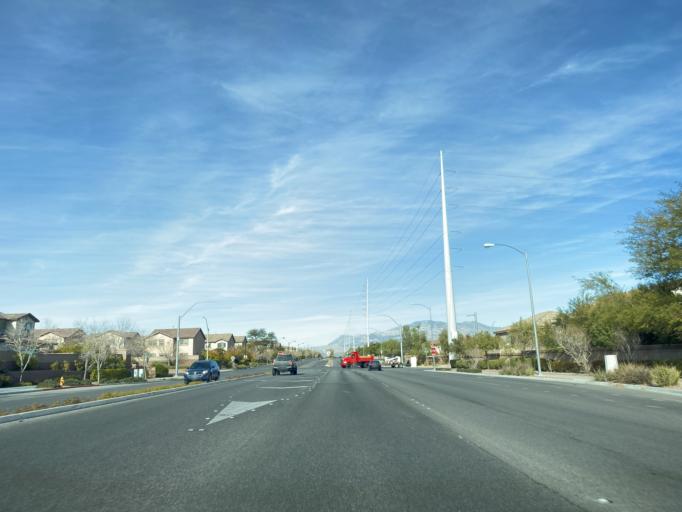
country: US
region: Nevada
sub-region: Clark County
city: Summerlin South
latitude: 36.2985
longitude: -115.3149
